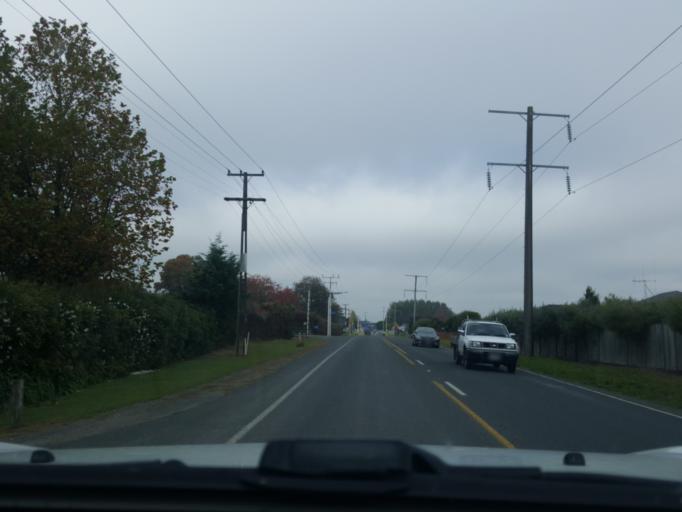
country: NZ
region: Waikato
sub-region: Hamilton City
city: Hamilton
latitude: -37.7439
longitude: 175.2912
